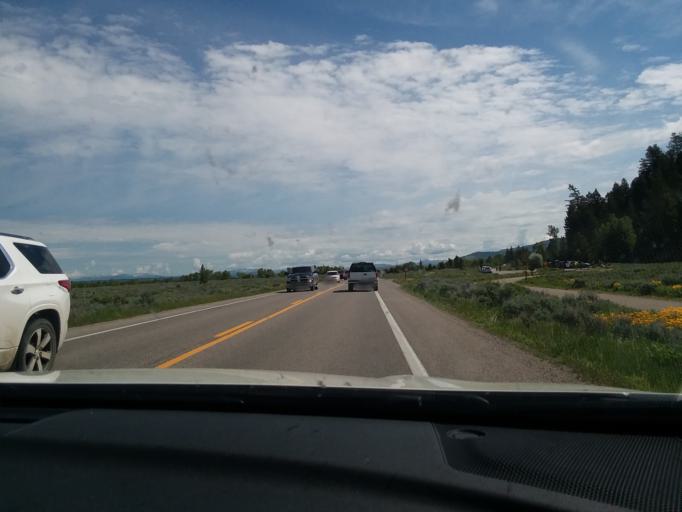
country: US
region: Wyoming
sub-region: Teton County
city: Jackson
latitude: 43.6605
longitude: -110.7003
